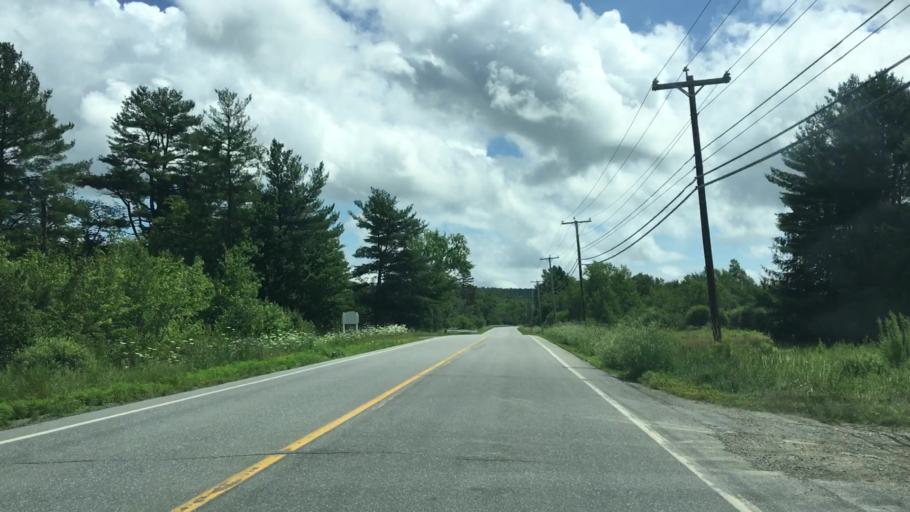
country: US
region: Maine
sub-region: Penobscot County
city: Hermon
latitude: 44.8087
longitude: -68.9762
